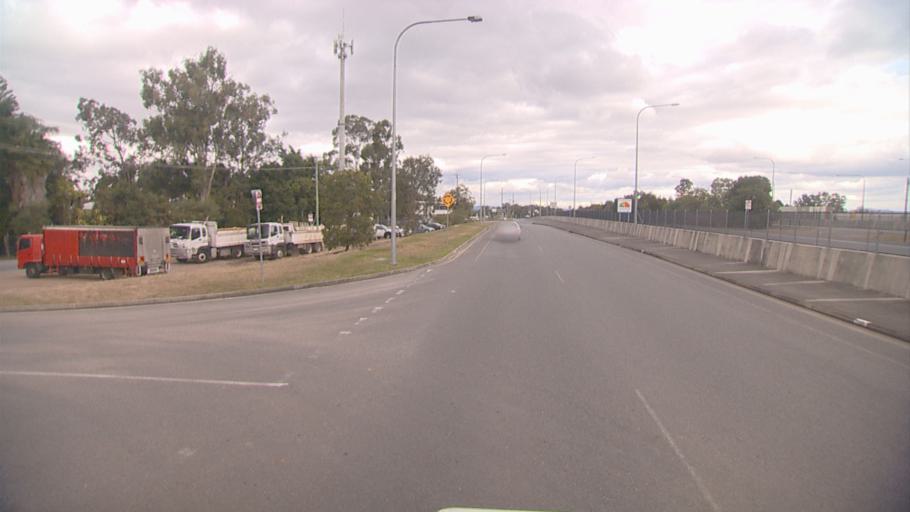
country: AU
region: Queensland
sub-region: Logan
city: Park Ridge South
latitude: -27.7048
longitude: 153.0385
